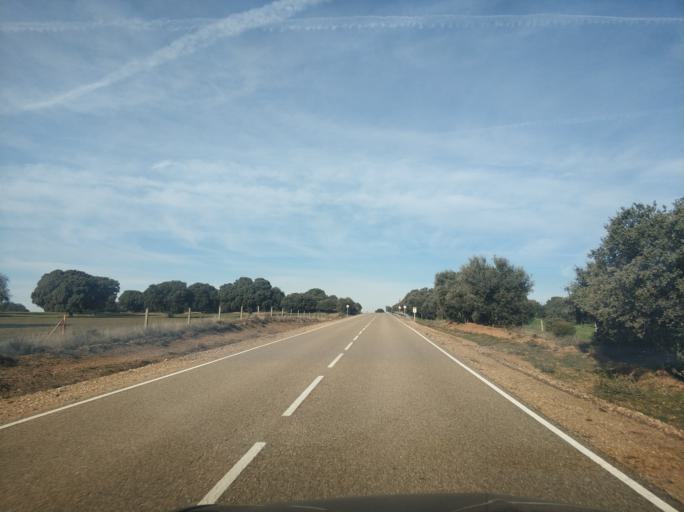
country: ES
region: Castille and Leon
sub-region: Provincia de Salamanca
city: Zarapicos
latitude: 41.0059
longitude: -5.8351
